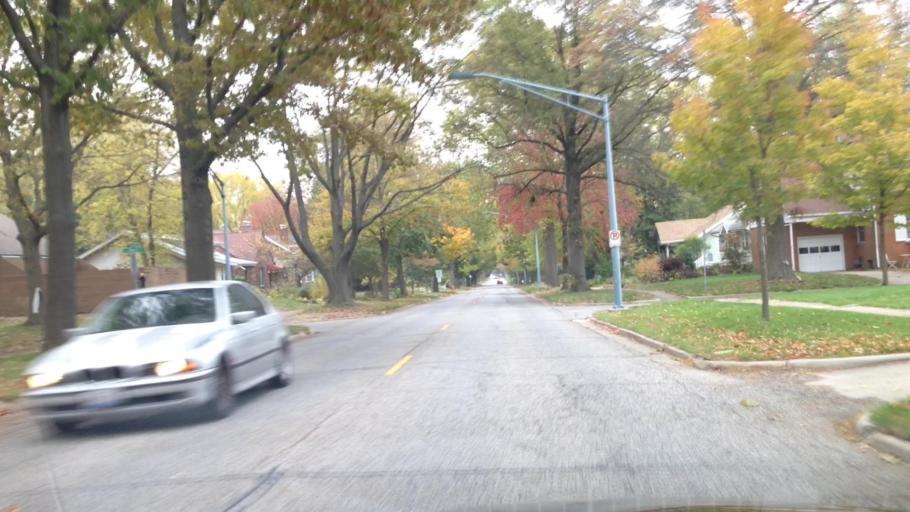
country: US
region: Illinois
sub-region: Champaign County
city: Champaign
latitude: 40.1102
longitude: -88.2654
